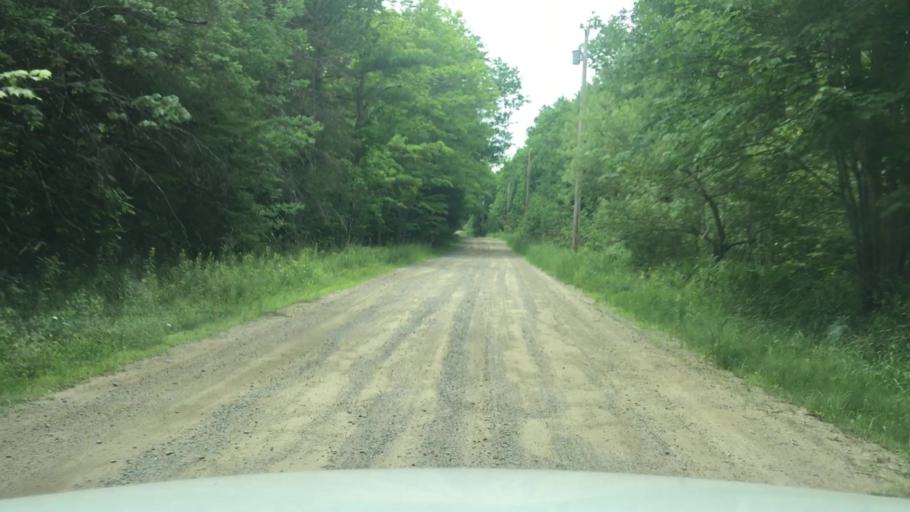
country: US
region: Maine
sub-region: Waldo County
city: Searsmont
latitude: 44.4258
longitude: -69.2568
